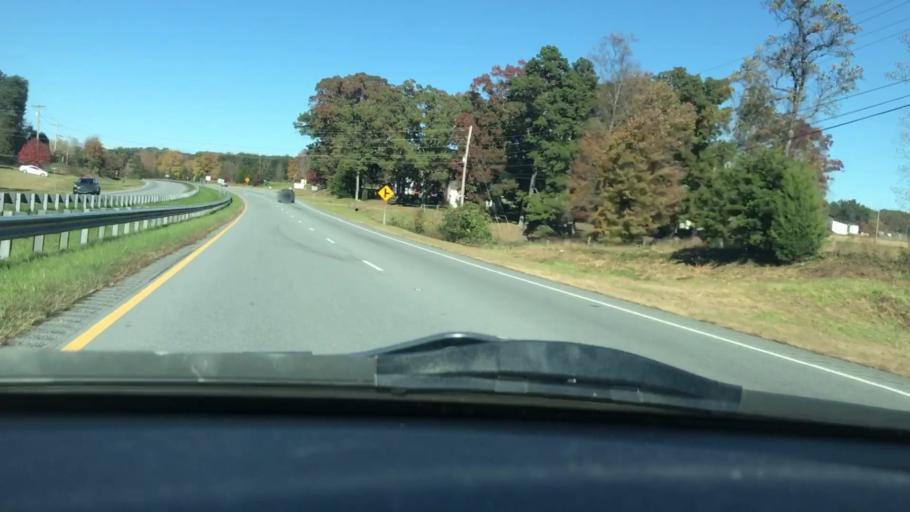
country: US
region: North Carolina
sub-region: Rockingham County
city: Madison
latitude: 36.3367
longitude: -79.9443
